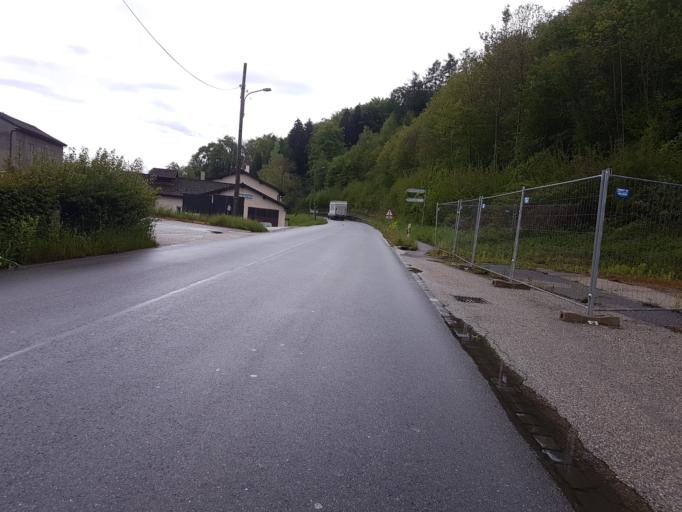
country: CH
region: Vaud
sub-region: Gros-de-Vaud District
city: Penthalaz
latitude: 46.6013
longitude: 6.5247
